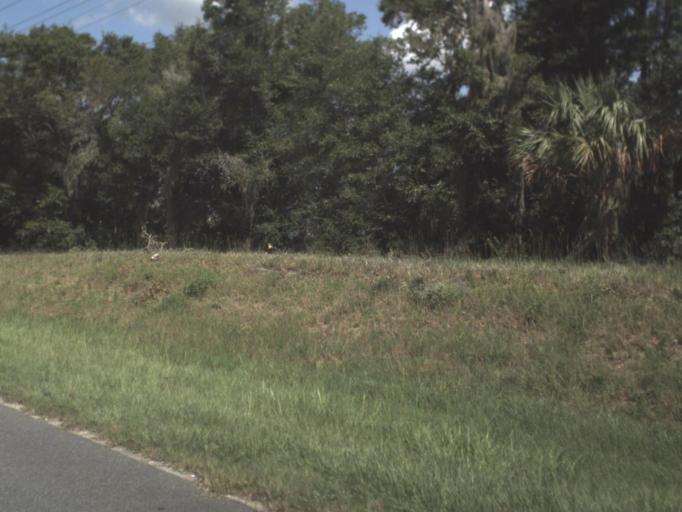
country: US
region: Florida
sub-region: Putnam County
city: Interlachen
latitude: 29.7276
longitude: -81.9222
